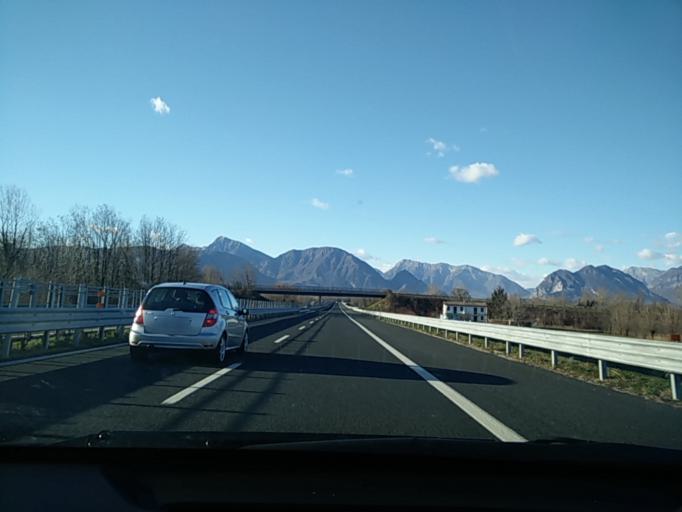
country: IT
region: Friuli Venezia Giulia
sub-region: Provincia di Udine
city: Buia
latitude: 46.1988
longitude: 13.1009
